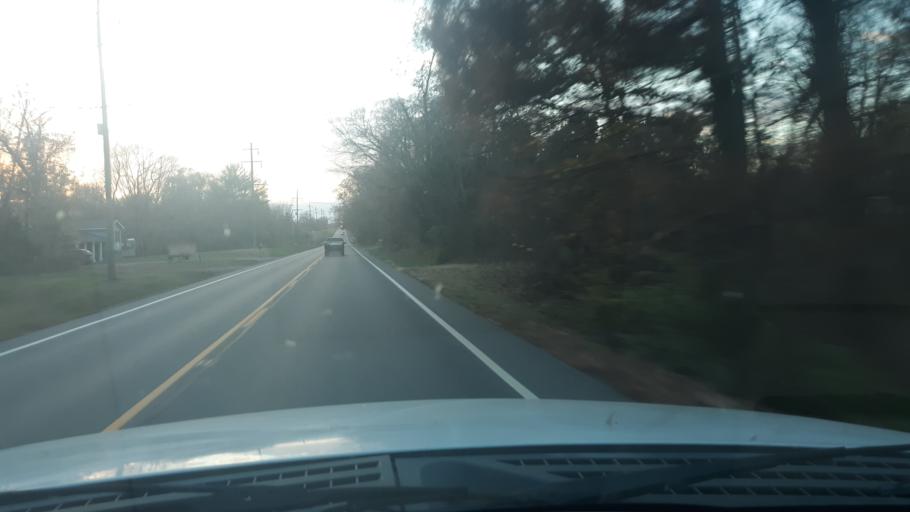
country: US
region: Illinois
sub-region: Saline County
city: Harrisburg
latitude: 37.8347
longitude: -88.5531
